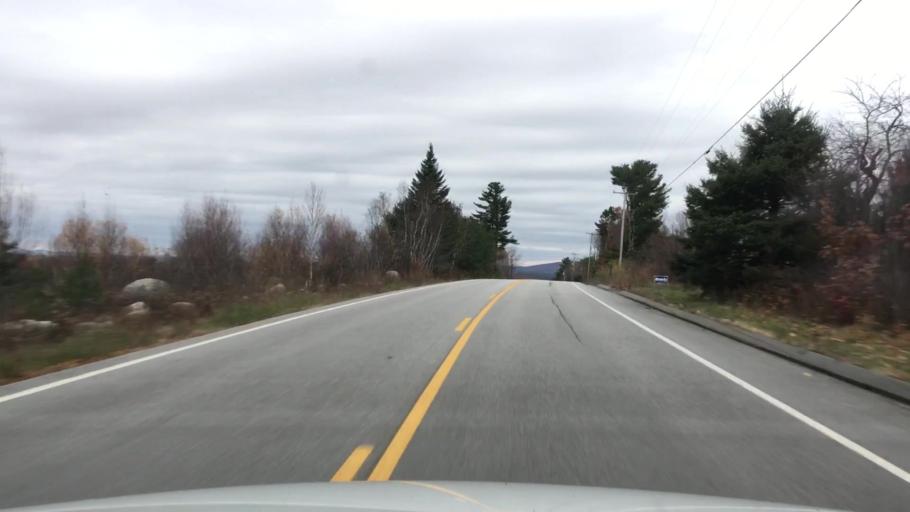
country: US
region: Maine
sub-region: Hancock County
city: Orland
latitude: 44.5462
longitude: -68.6884
